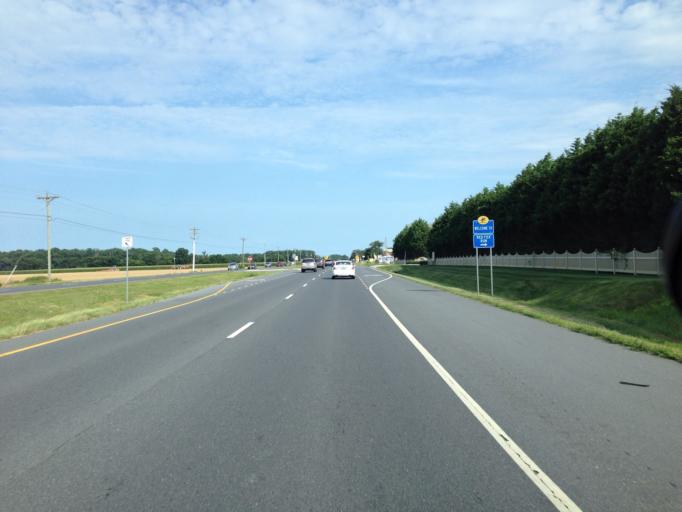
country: US
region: Delaware
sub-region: Sussex County
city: Lewes
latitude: 38.7705
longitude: -75.2191
